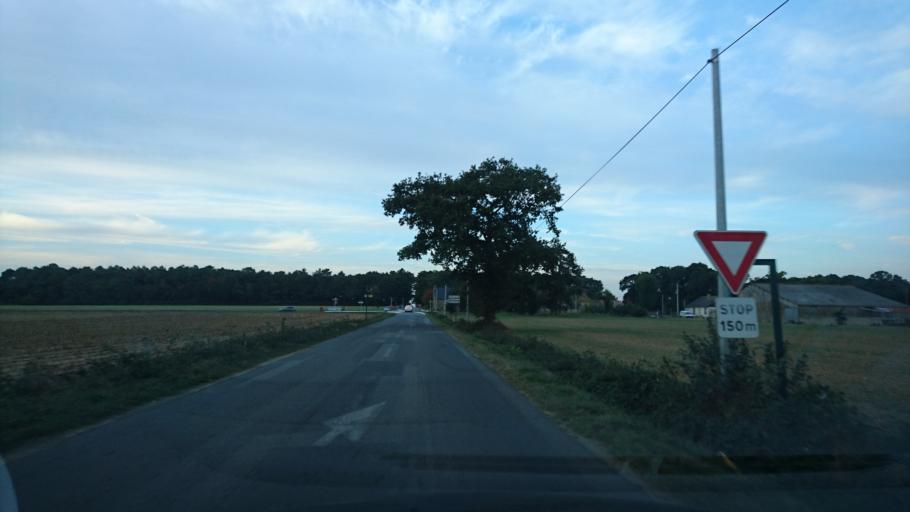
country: FR
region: Brittany
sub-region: Departement d'Ille-et-Vilaine
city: Saint-Just
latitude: 47.7940
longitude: -2.0090
